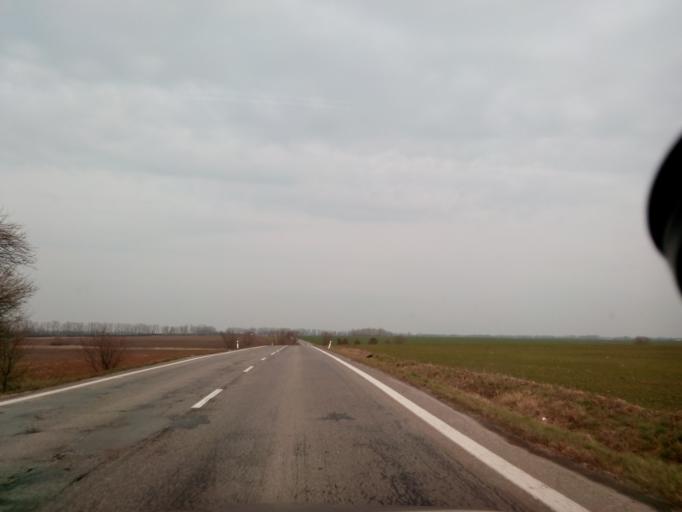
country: SK
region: Kosicky
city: Trebisov
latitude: 48.5339
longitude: 21.6767
